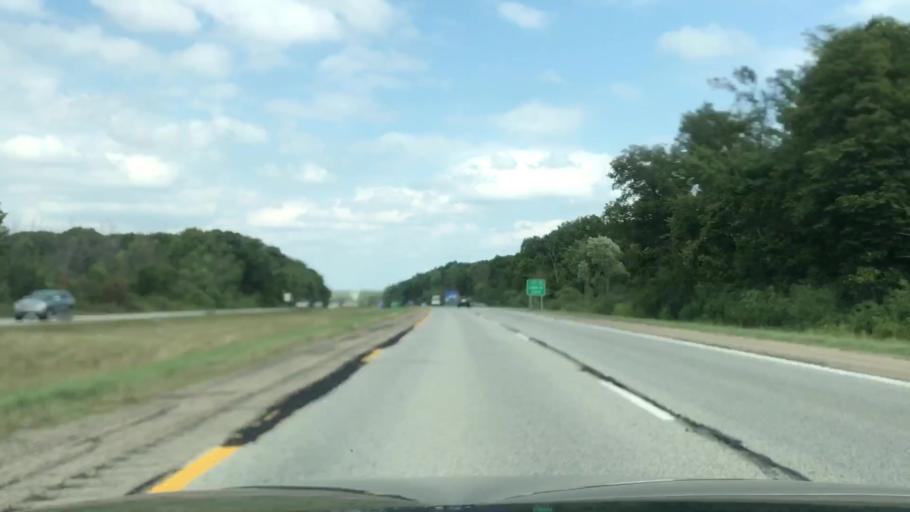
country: US
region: Michigan
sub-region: Ottawa County
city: Jenison
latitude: 42.8686
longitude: -85.7948
